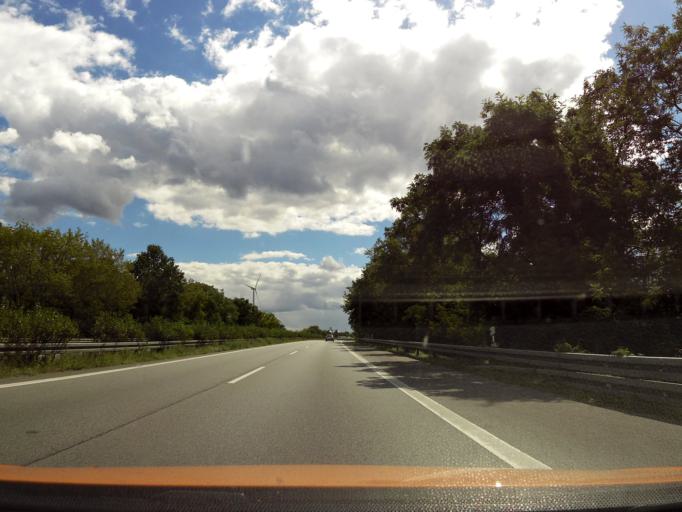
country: DE
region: Berlin
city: Blankenfelde
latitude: 52.6725
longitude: 13.4004
